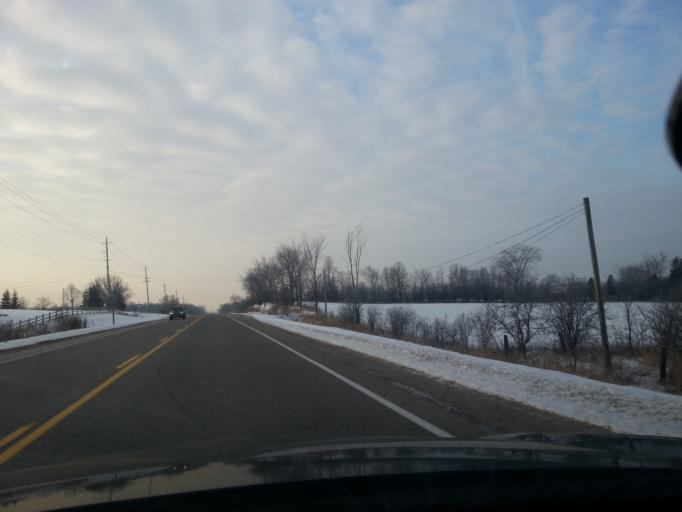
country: CA
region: Ontario
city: Perth
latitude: 44.9550
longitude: -76.2343
